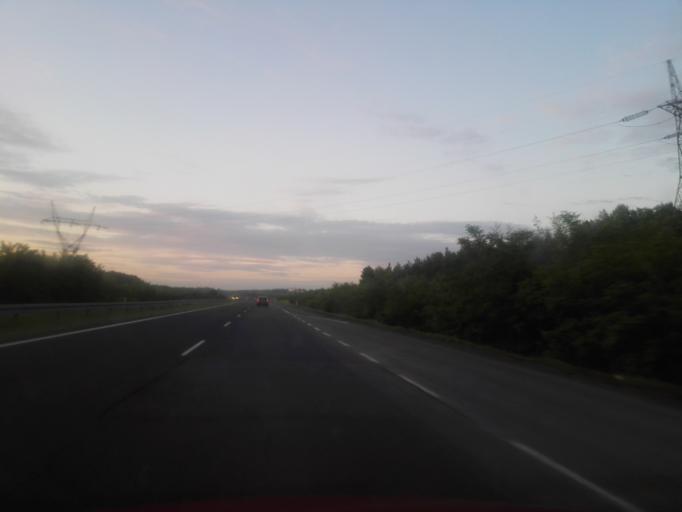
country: PL
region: Lodz Voivodeship
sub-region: Powiat radomszczanski
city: Radomsko
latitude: 51.0468
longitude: 19.3502
